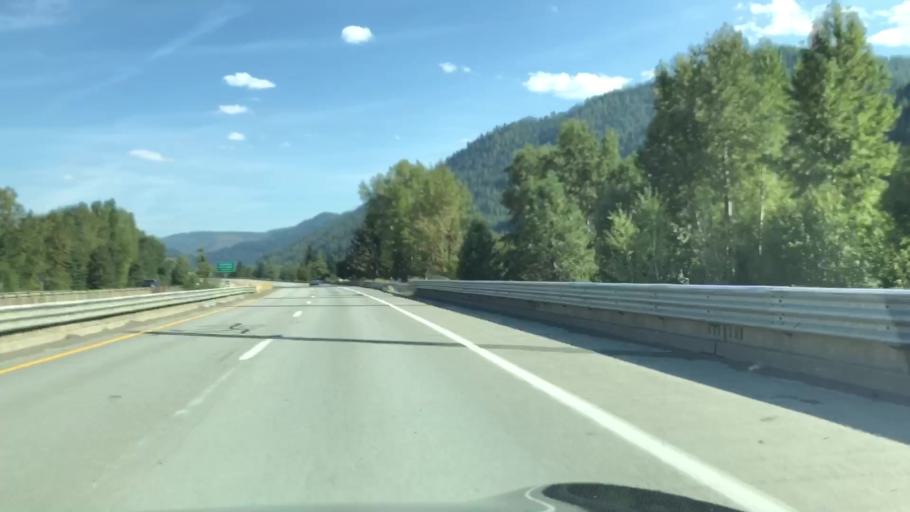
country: US
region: Idaho
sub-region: Shoshone County
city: Osburn
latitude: 47.5168
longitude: -116.0338
